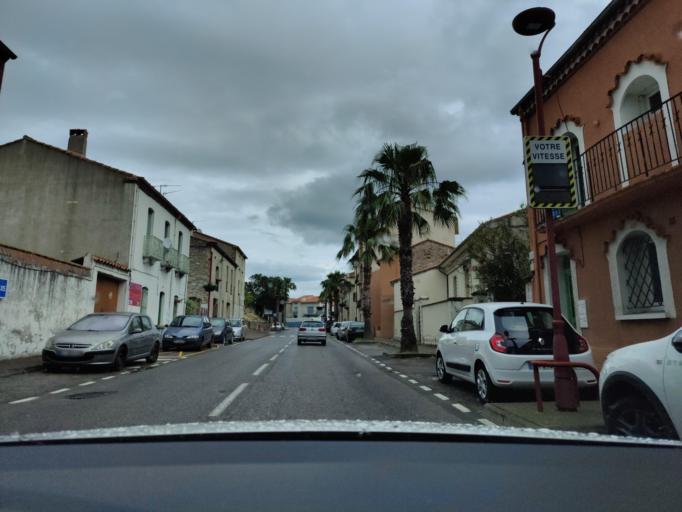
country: FR
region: Languedoc-Roussillon
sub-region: Departement des Pyrenees-Orientales
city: el Volo
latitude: 42.5210
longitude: 2.8318
